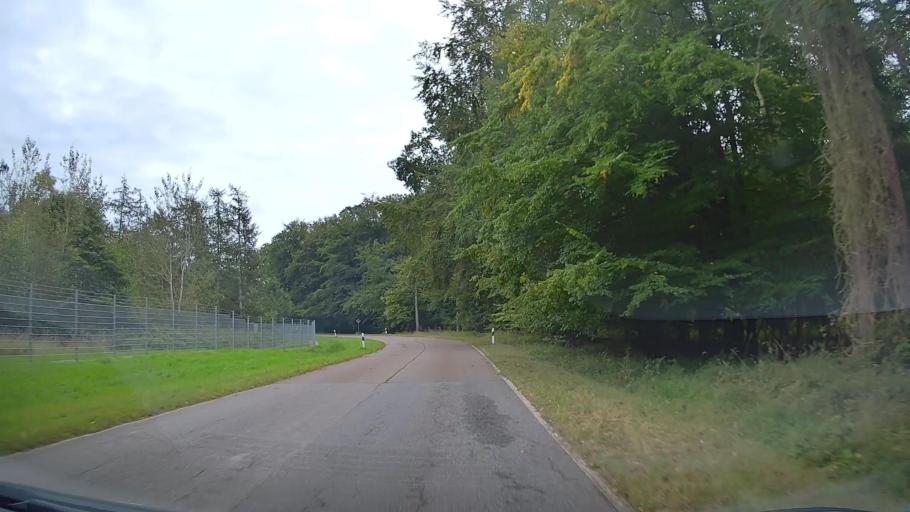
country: DE
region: Schleswig-Holstein
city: Panker
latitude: 54.3634
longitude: 10.5717
